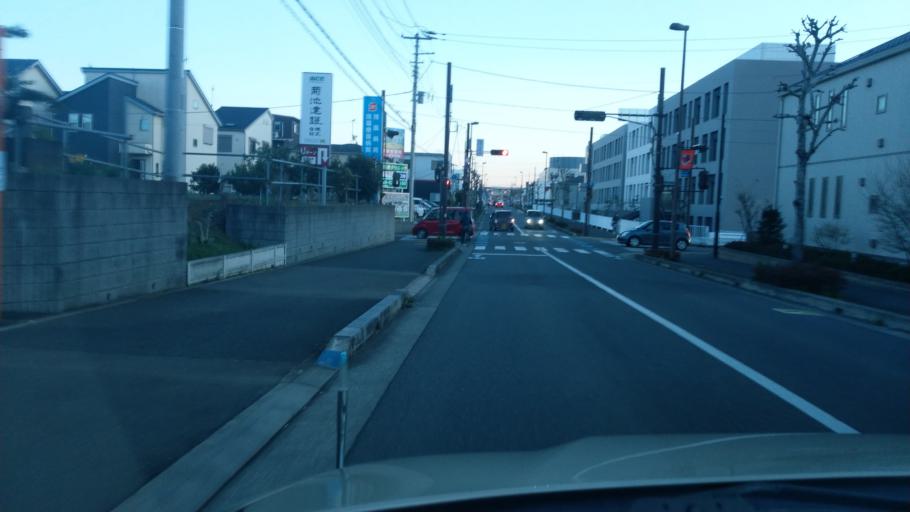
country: JP
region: Saitama
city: Ageoshimo
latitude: 35.9274
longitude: 139.5799
